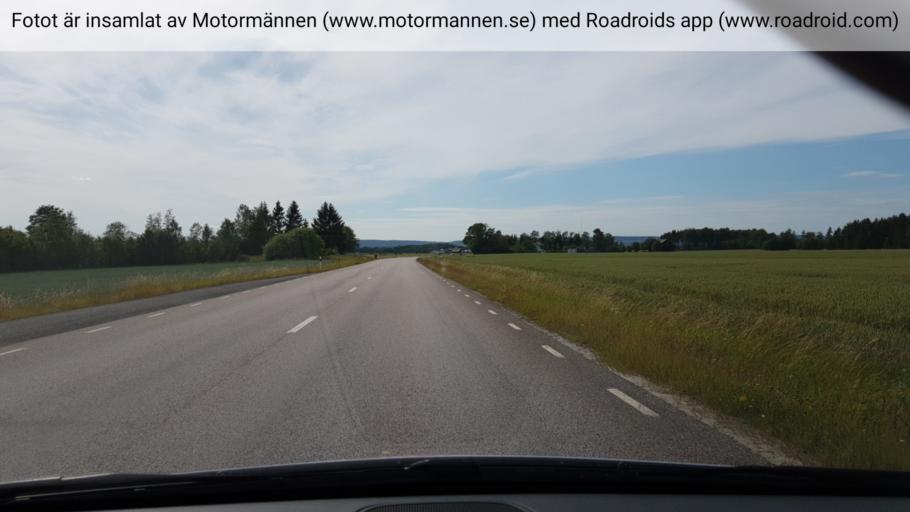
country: SE
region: Vaestra Goetaland
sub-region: Tidaholms Kommun
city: Olofstorp
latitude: 58.3723
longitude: 13.9960
